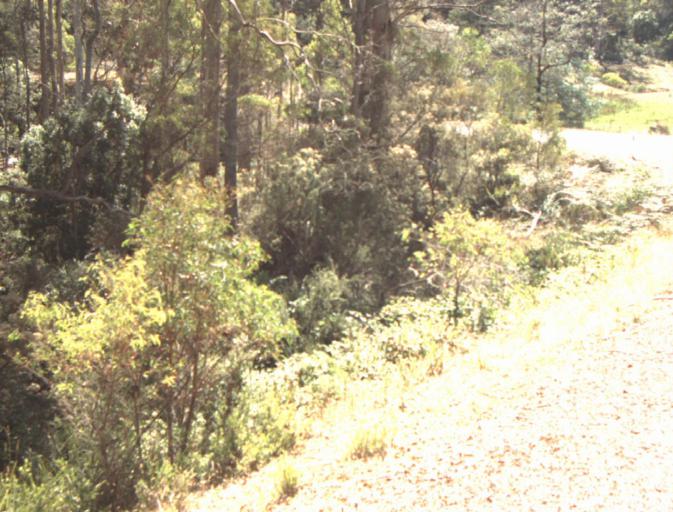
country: AU
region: Tasmania
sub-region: Launceston
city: Newstead
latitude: -41.3097
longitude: 147.3357
